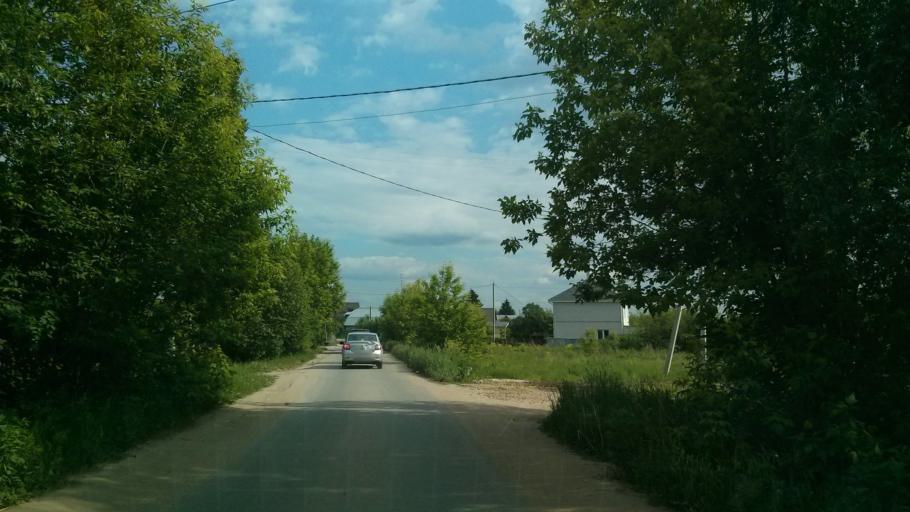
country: RU
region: Nizjnij Novgorod
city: Afonino
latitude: 56.2806
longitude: 44.1022
